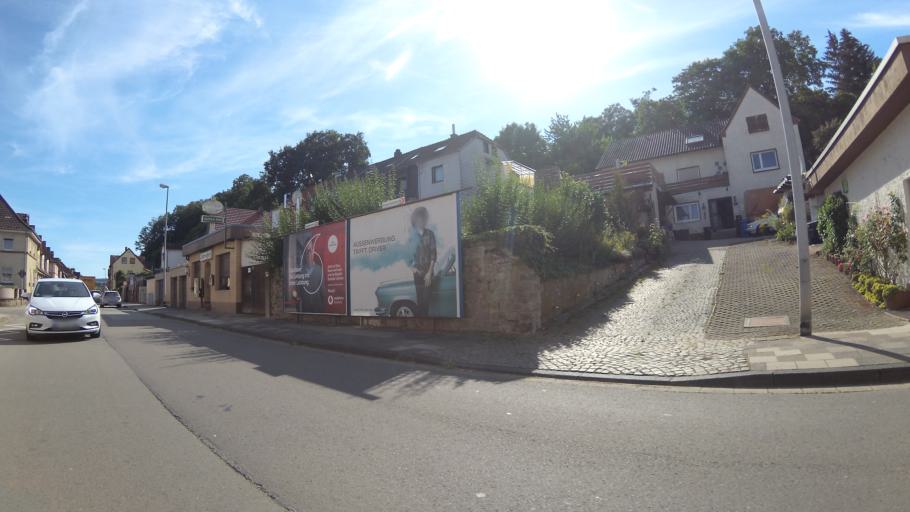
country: DE
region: Rheinland-Pfalz
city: Zweibrucken
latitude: 49.2406
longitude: 7.3574
